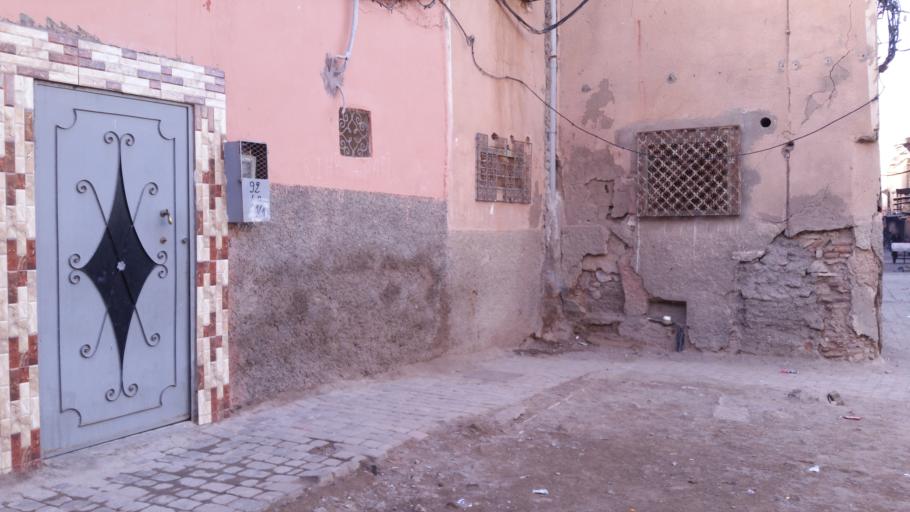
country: MA
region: Marrakech-Tensift-Al Haouz
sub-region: Marrakech
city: Marrakesh
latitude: 31.6180
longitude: -7.9821
